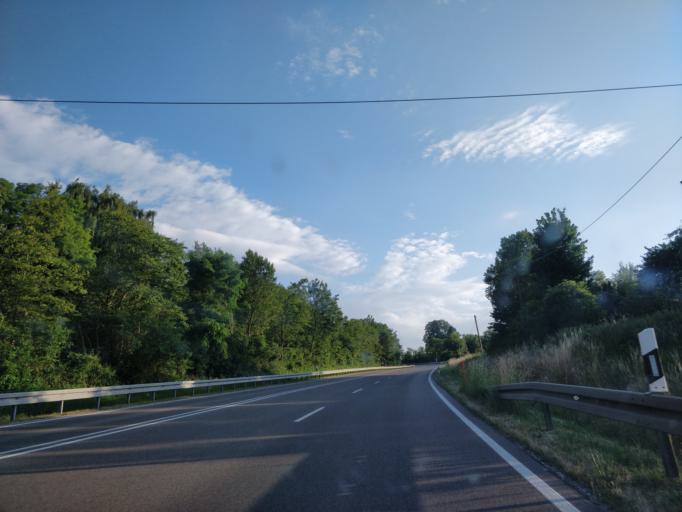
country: DE
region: Bavaria
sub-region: Swabia
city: Ederheim
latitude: 48.8214
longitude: 10.4613
